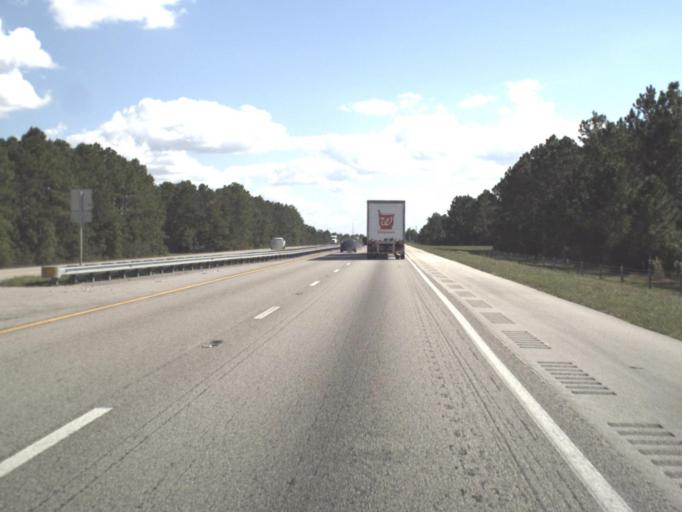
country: US
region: Florida
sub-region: Brevard County
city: June Park
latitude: 27.9032
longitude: -81.0457
